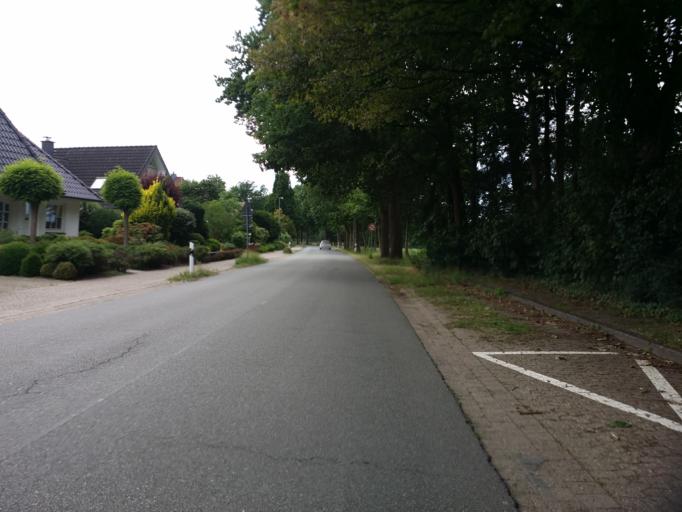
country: DE
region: Lower Saxony
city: Stuhr
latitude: 53.0283
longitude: 8.7241
